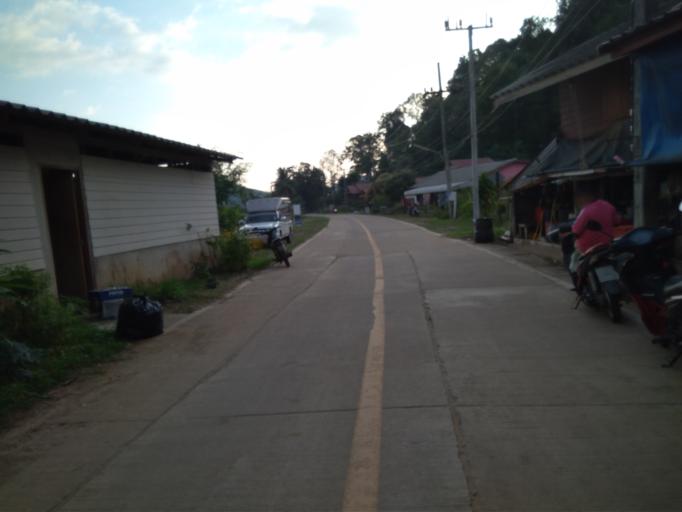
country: TH
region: Phangnga
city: Ko Yao
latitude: 8.1349
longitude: 98.6263
